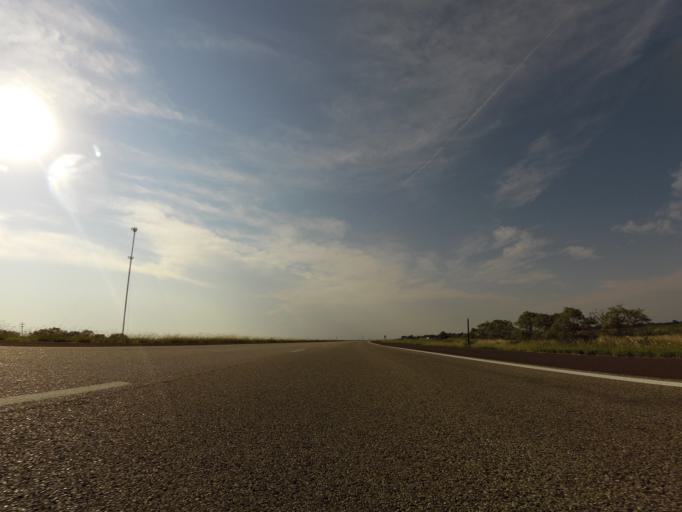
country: US
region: Kansas
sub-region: Reno County
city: South Hutchinson
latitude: 37.9701
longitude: -97.9345
